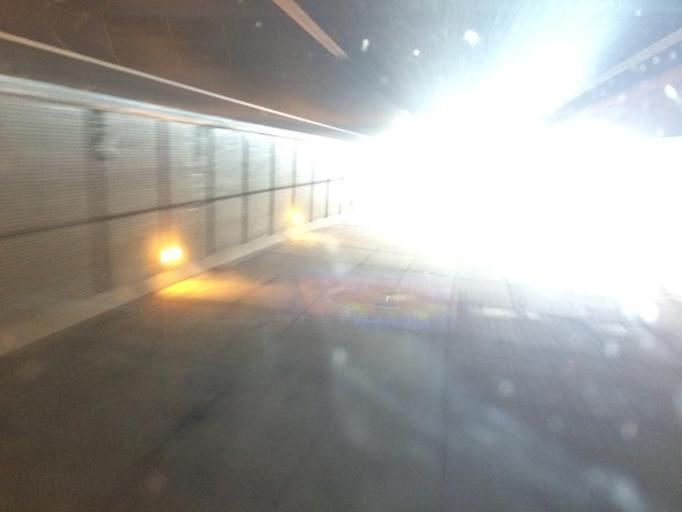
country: ES
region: Madrid
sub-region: Provincia de Madrid
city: Barajas de Madrid
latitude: 40.4675
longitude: -3.5820
